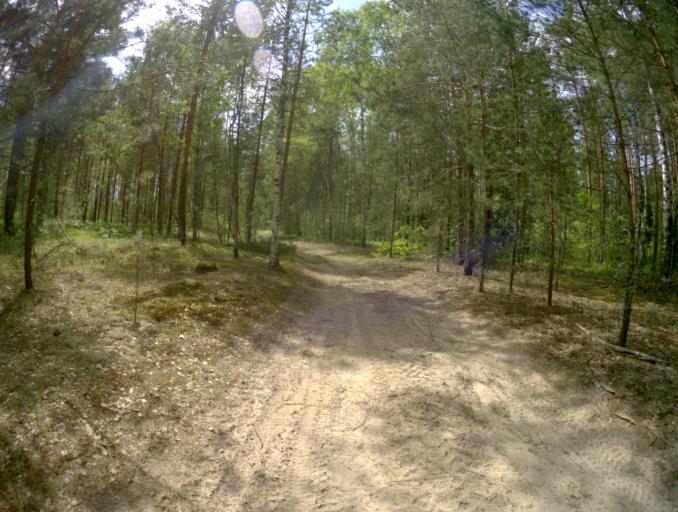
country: RU
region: Vladimir
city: Ivanishchi
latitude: 55.6926
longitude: 40.4241
